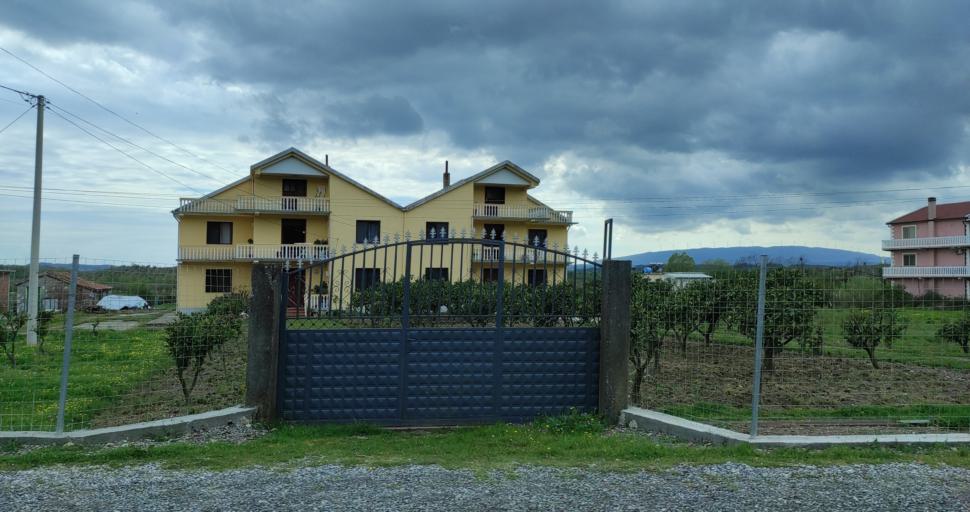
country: AL
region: Shkoder
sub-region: Rrethi i Shkodres
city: Dajc
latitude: 42.0185
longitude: 19.3847
